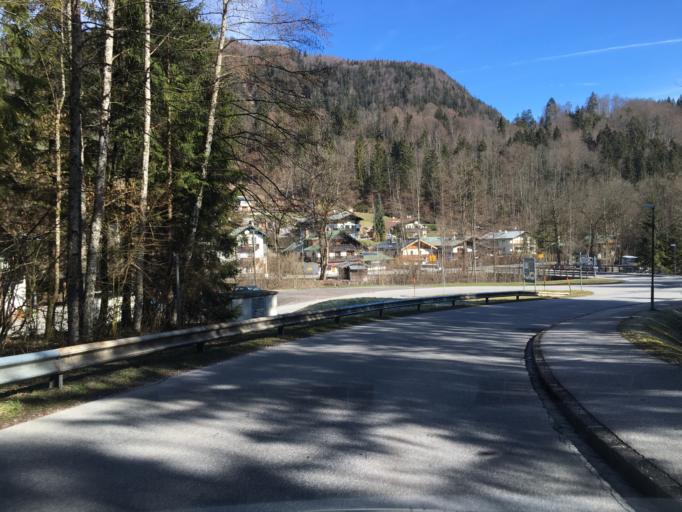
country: DE
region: Bavaria
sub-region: Upper Bavaria
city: Bischofswiesen
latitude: 47.6131
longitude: 12.9521
